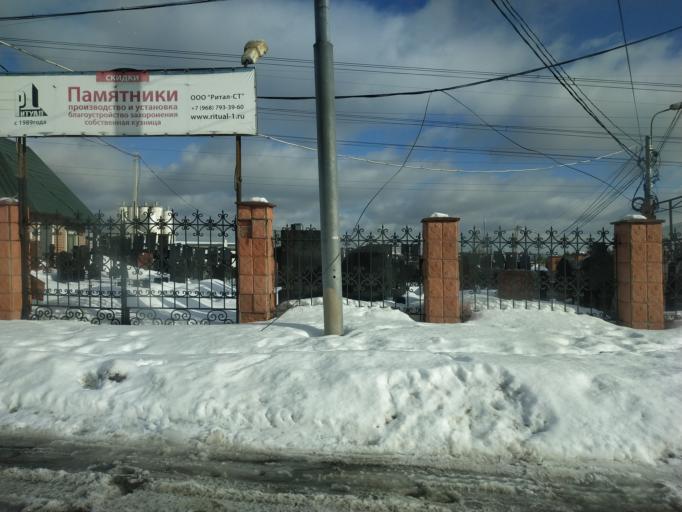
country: RU
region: Moskovskaya
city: Mosrentgen
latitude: 55.6074
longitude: 37.4490
